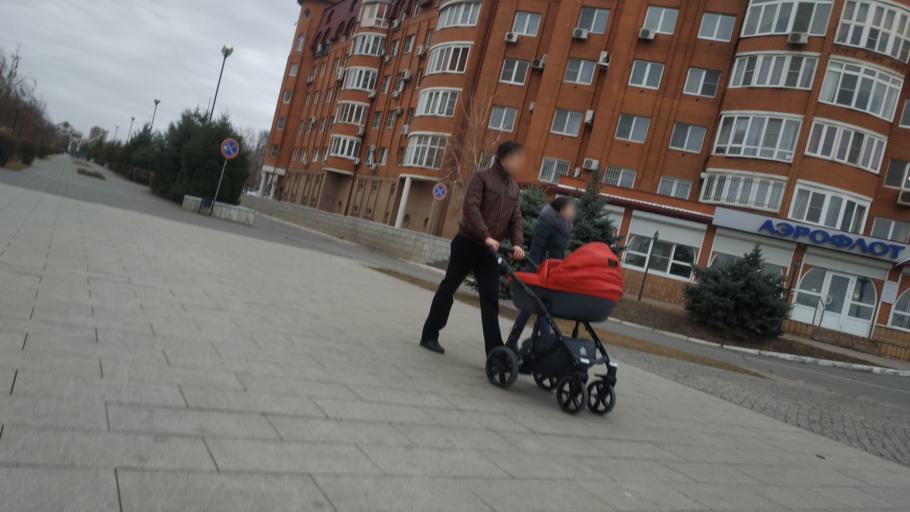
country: RU
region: Astrakhan
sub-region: Gorod Astrakhan'
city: Astrakhan'
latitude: 46.3469
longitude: 48.0165
